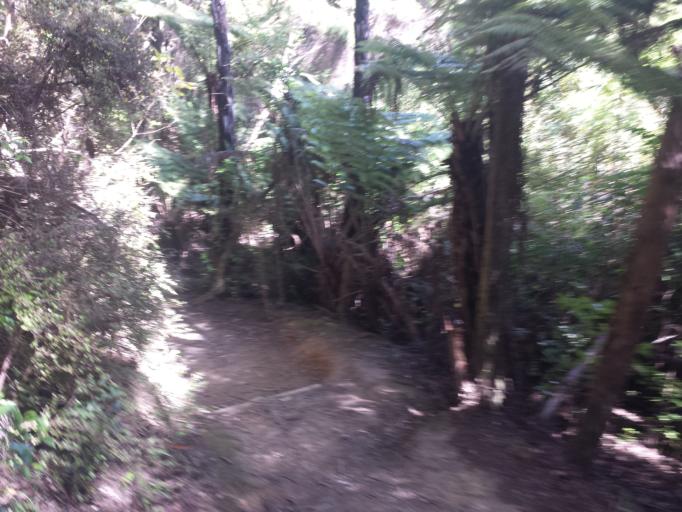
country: NZ
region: Northland
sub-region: Far North District
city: Paihia
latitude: -35.3032
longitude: 174.1055
